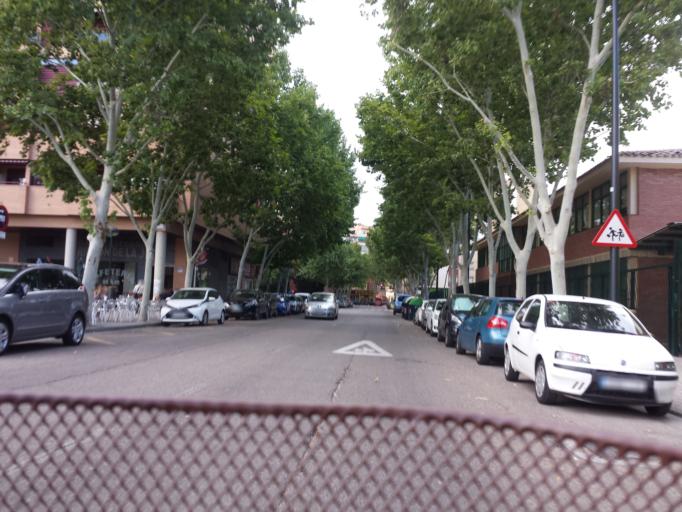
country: ES
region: Aragon
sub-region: Provincia de Zaragoza
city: Zaragoza
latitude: 41.6597
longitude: -0.8588
